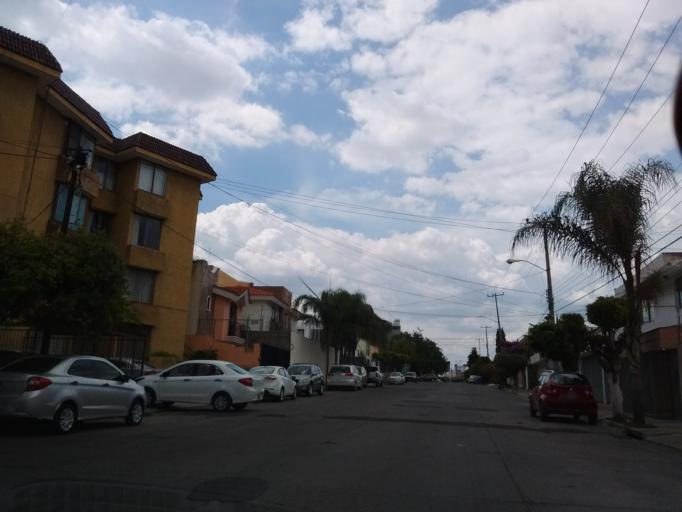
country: MX
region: Jalisco
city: Guadalajara
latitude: 20.6536
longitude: -103.3868
